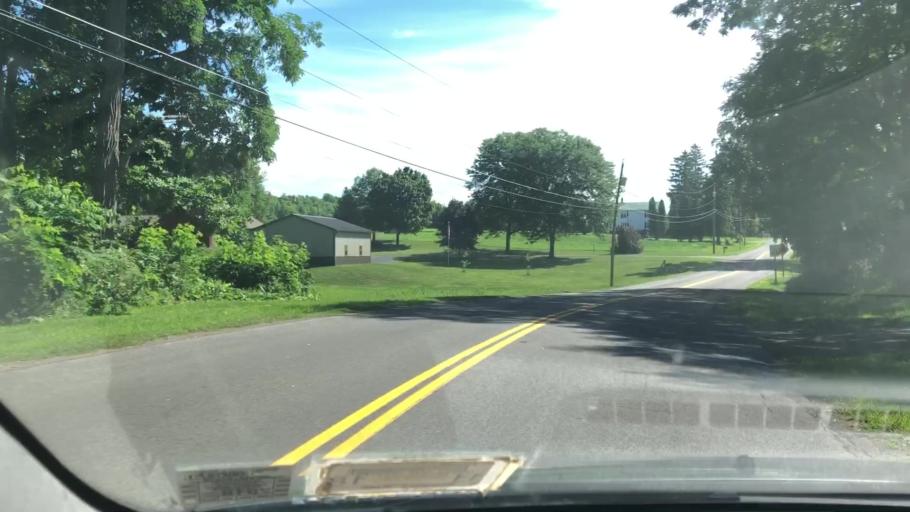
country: US
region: New York
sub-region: Monroe County
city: Fairport
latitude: 43.1281
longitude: -77.3686
